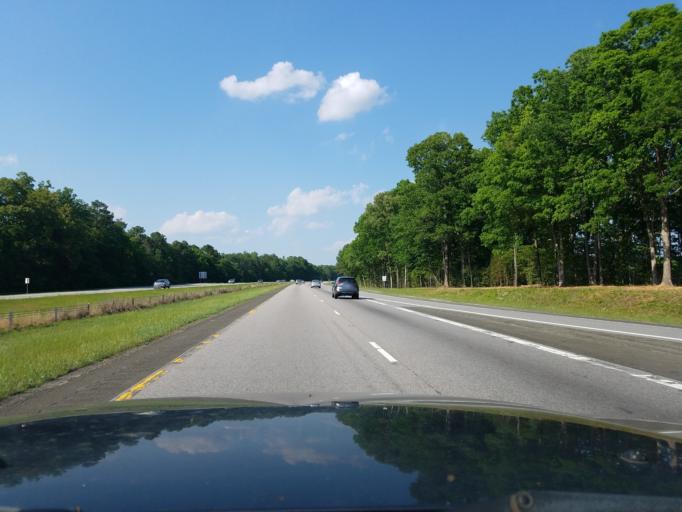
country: US
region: North Carolina
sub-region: Granville County
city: Butner
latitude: 36.1227
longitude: -78.7446
